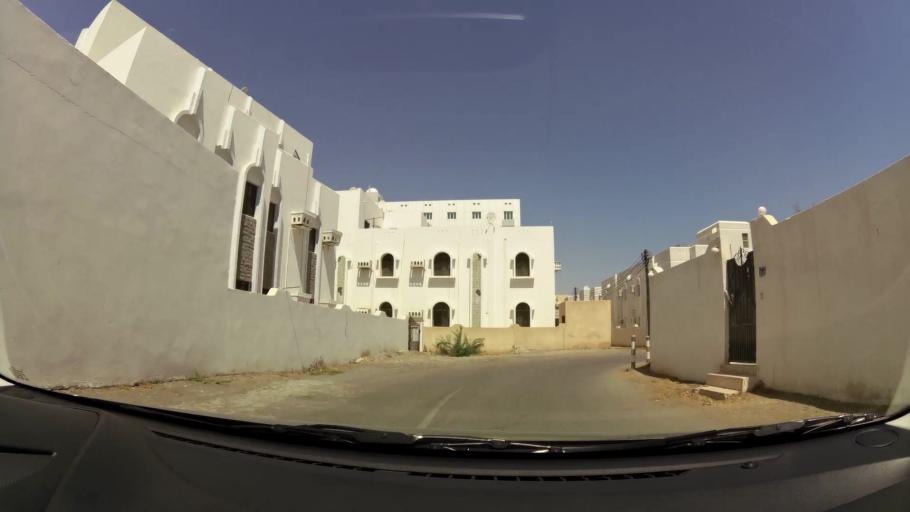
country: OM
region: Muhafazat Masqat
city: Bawshar
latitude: 23.5875
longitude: 58.3978
